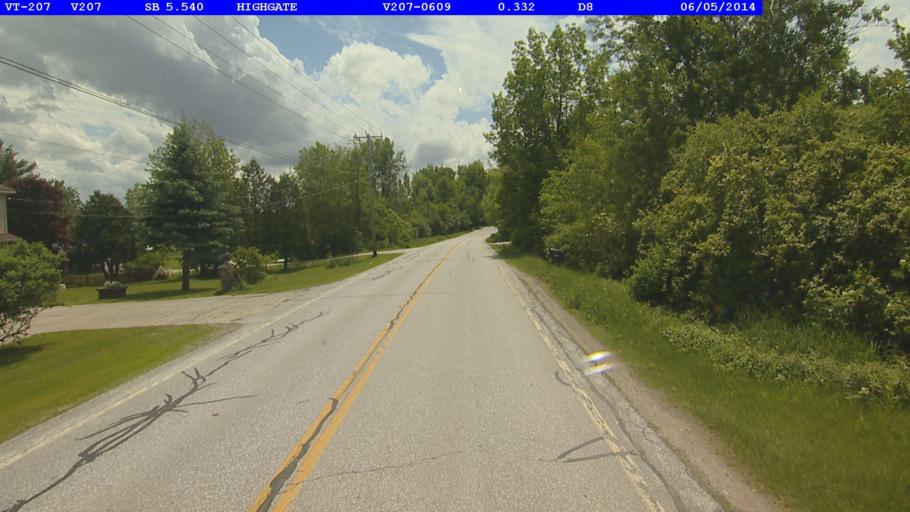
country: US
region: Vermont
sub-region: Franklin County
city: Swanton
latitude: 44.9161
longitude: -73.0562
